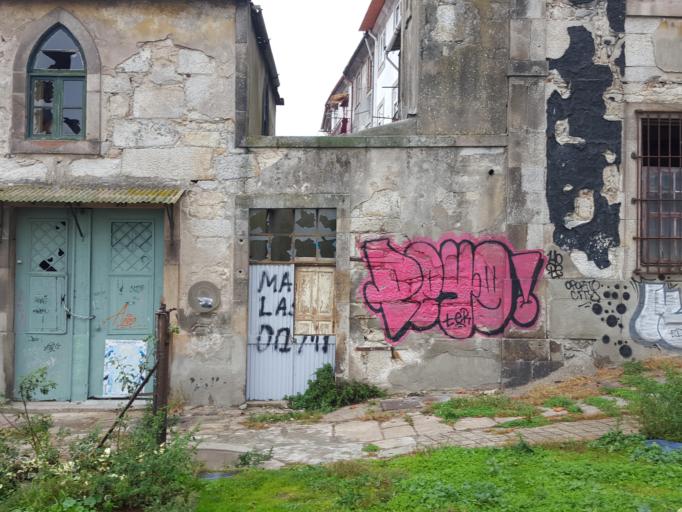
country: PT
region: Porto
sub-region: Porto
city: Porto
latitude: 41.1431
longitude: -8.6158
